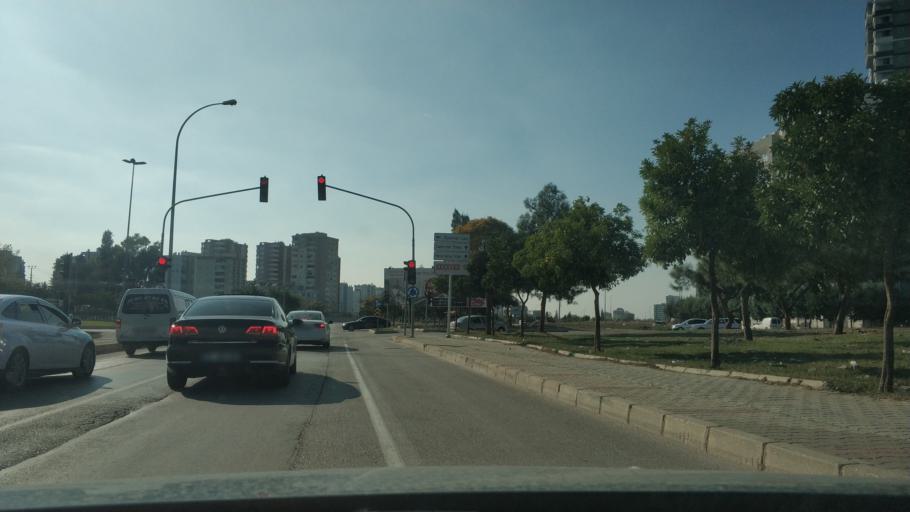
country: TR
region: Adana
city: Seyhan
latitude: 37.0104
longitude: 35.2731
